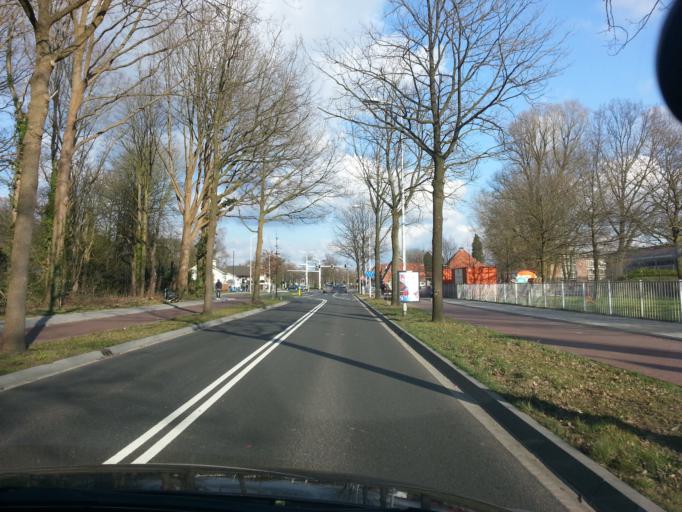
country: NL
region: North Brabant
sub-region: Gemeente Eindhoven
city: Eindhoven
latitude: 51.4168
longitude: 5.4810
